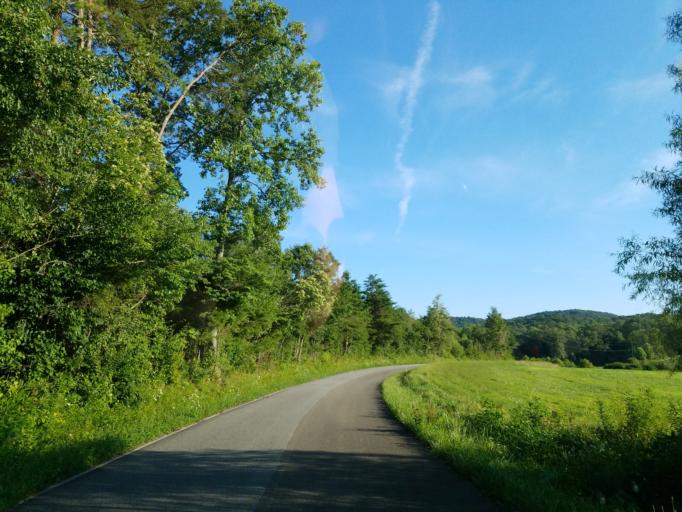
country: US
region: Georgia
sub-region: Pickens County
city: Jasper
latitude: 34.5994
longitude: -84.3220
